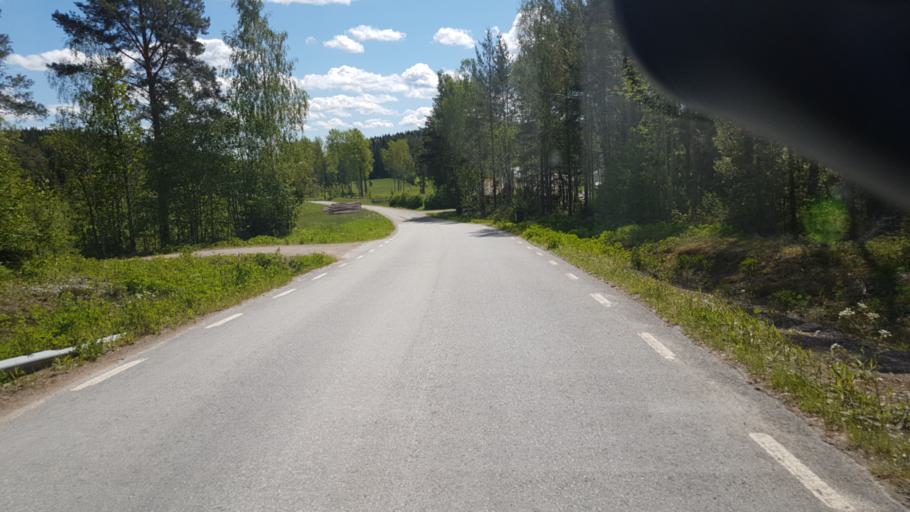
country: SE
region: Vaermland
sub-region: Arvika Kommun
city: Arvika
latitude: 59.6215
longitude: 12.8921
